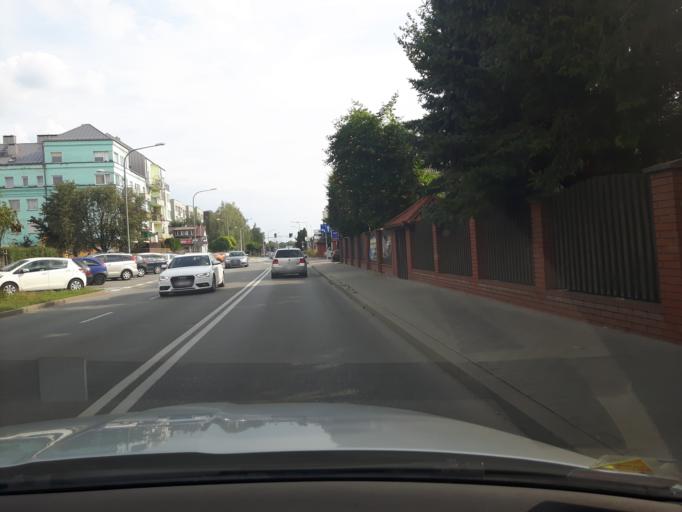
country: PL
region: Masovian Voivodeship
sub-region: Powiat piaseczynski
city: Piaseczno
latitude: 52.0805
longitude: 21.0153
